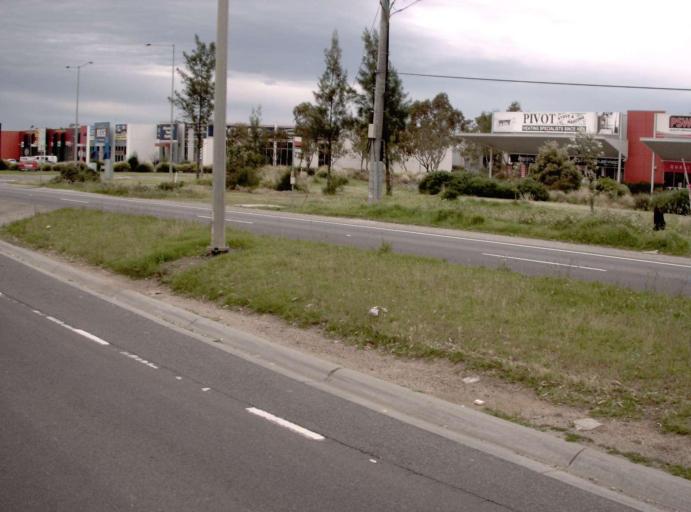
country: AU
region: Victoria
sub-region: Casey
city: Hampton Park
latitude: -38.0204
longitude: 145.2384
